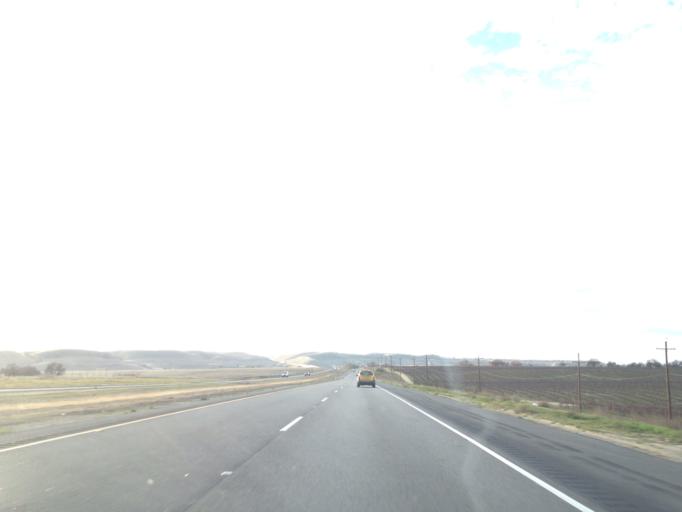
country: US
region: California
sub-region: San Luis Obispo County
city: Shandon
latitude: 35.6592
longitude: -120.4843
